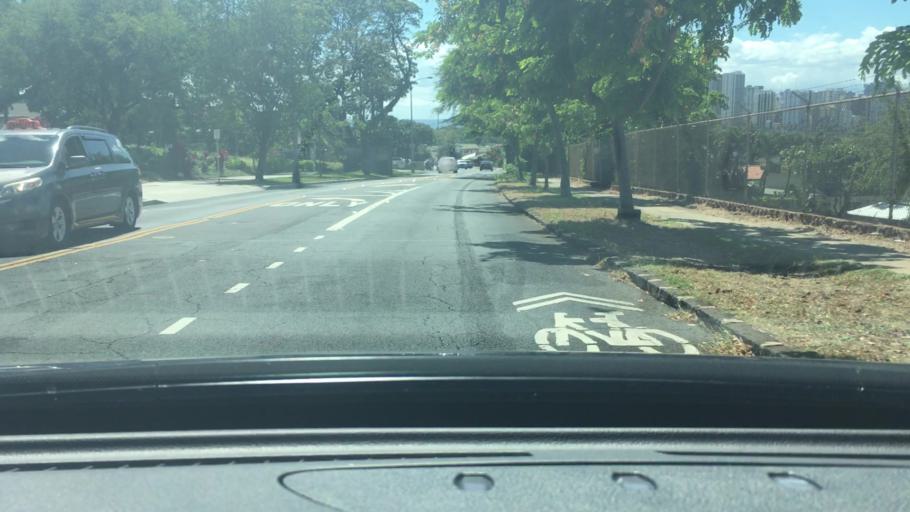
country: US
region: Hawaii
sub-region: Honolulu County
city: Honolulu
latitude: 21.2696
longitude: -157.8066
